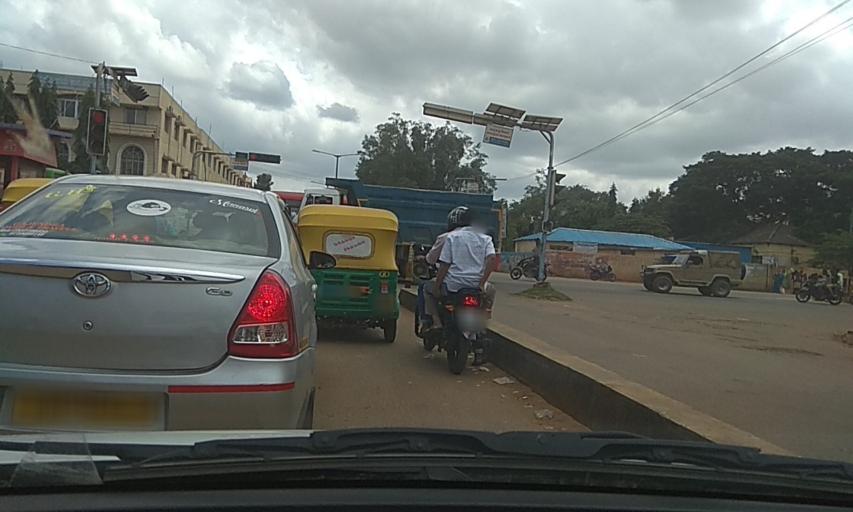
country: IN
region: Karnataka
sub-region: Tumkur
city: Tumkur
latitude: 13.3391
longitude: 77.0975
